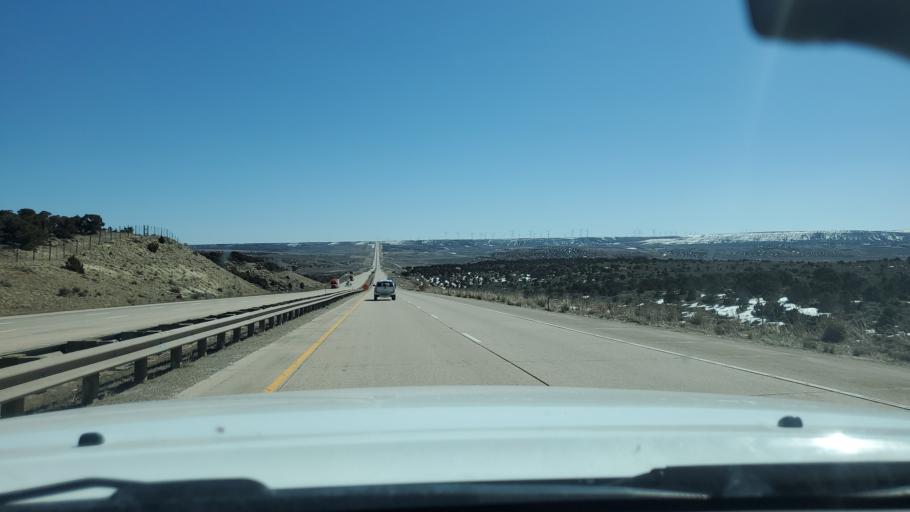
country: US
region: Wyoming
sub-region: Uinta County
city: Evanston
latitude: 41.2998
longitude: -110.6604
